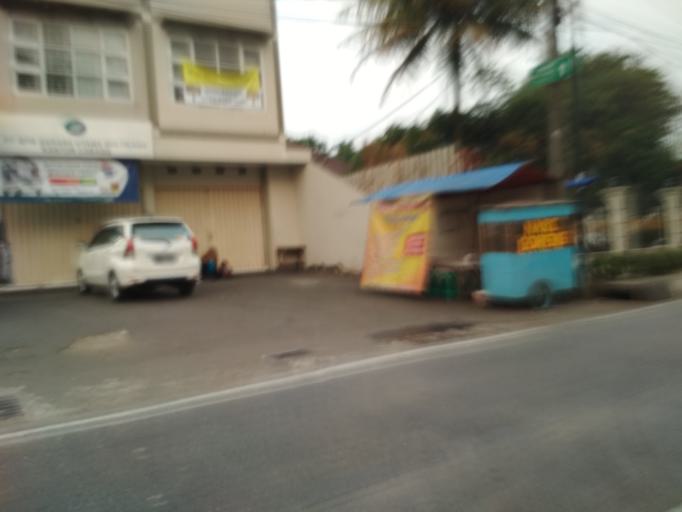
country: ID
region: West Java
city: Caringin
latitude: -6.6626
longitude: 106.8449
